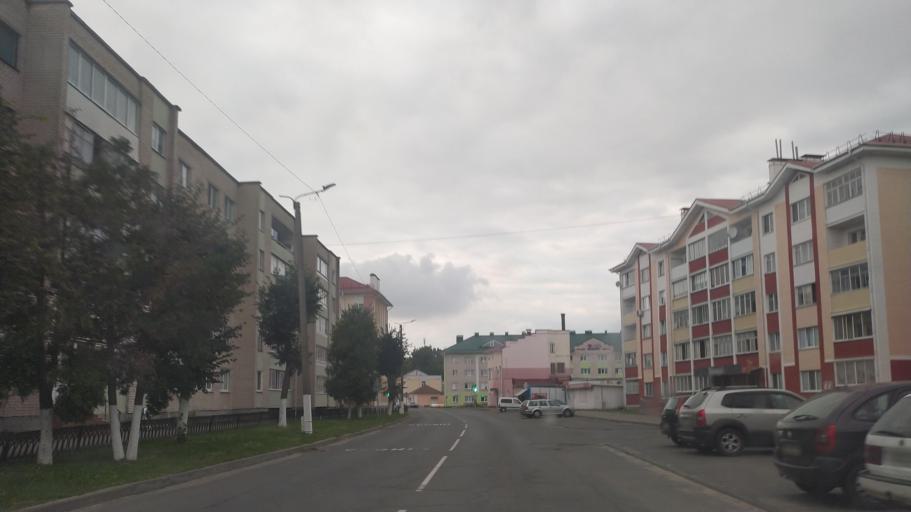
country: BY
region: Brest
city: Byaroza
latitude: 52.5327
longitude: 24.9844
